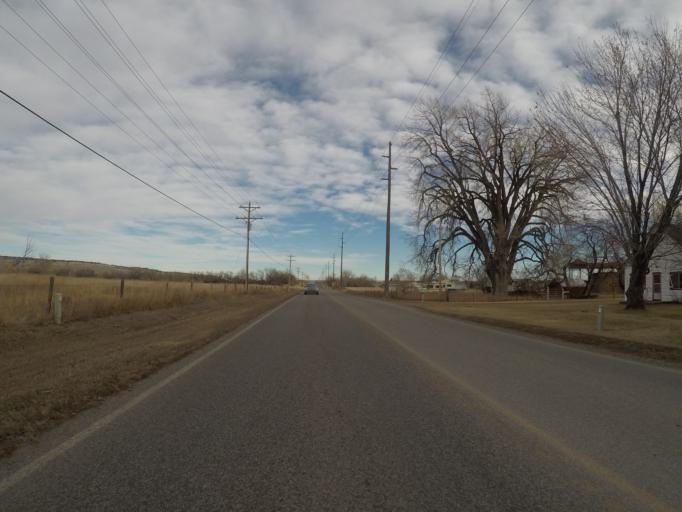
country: US
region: Montana
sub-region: Yellowstone County
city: Laurel
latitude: 45.7841
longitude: -108.6837
